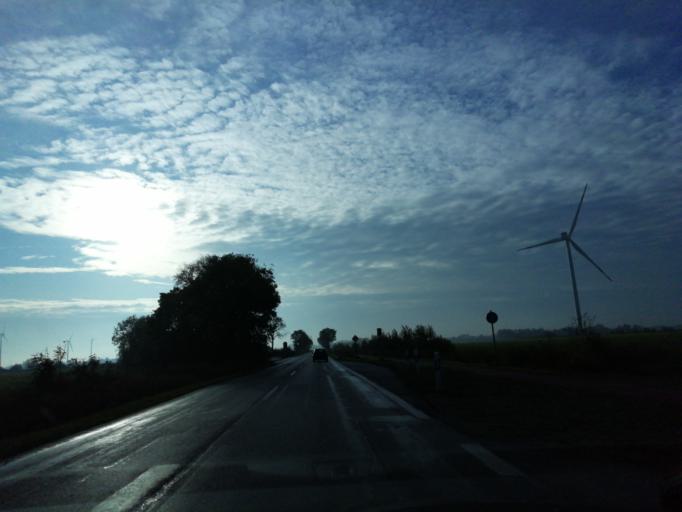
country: DE
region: Lower Saxony
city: Fedderwarden
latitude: 53.6113
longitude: 8.0418
